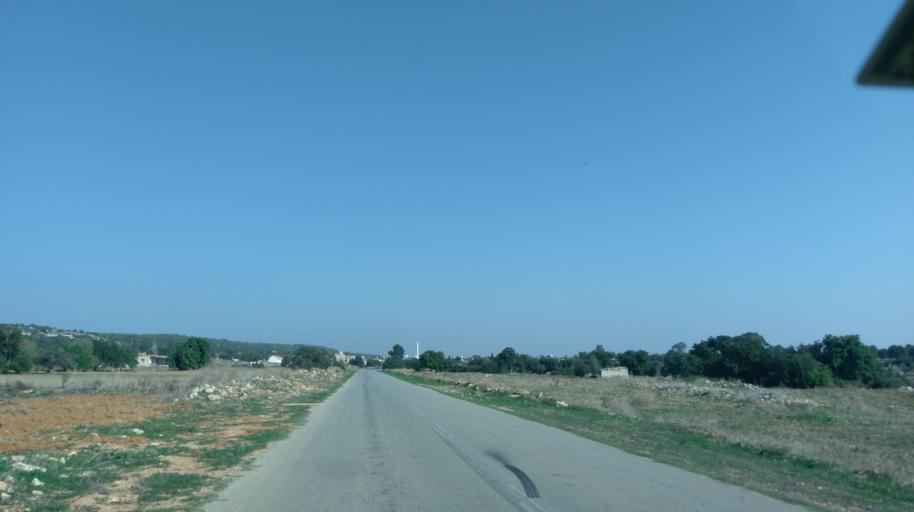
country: CY
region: Ammochostos
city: Leonarisso
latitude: 35.4754
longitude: 34.1585
